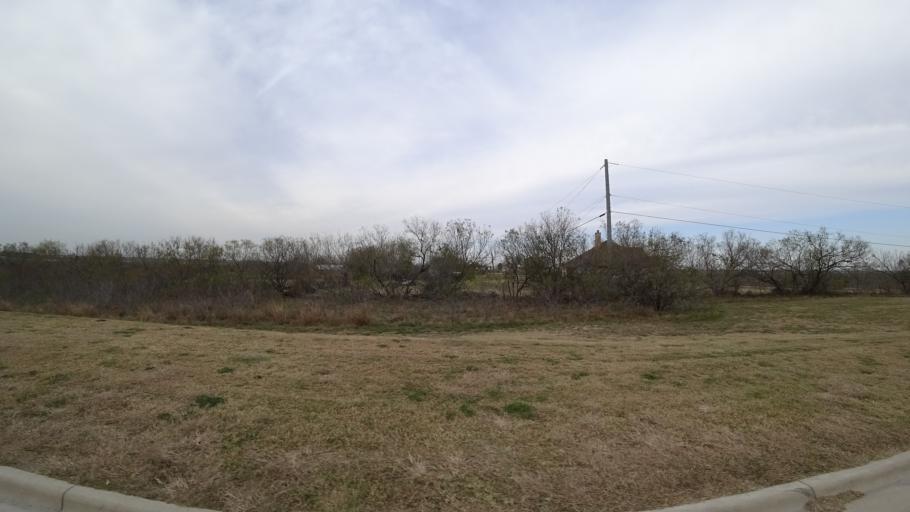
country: US
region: Texas
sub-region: Travis County
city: Garfield
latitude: 30.1447
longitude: -97.6248
